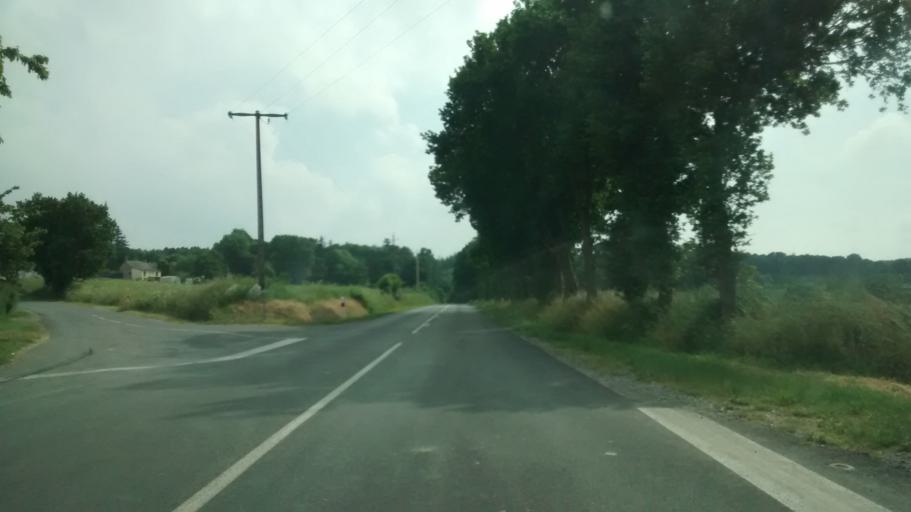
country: FR
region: Brittany
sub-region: Departement du Morbihan
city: Guer
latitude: 47.8990
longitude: -2.1474
